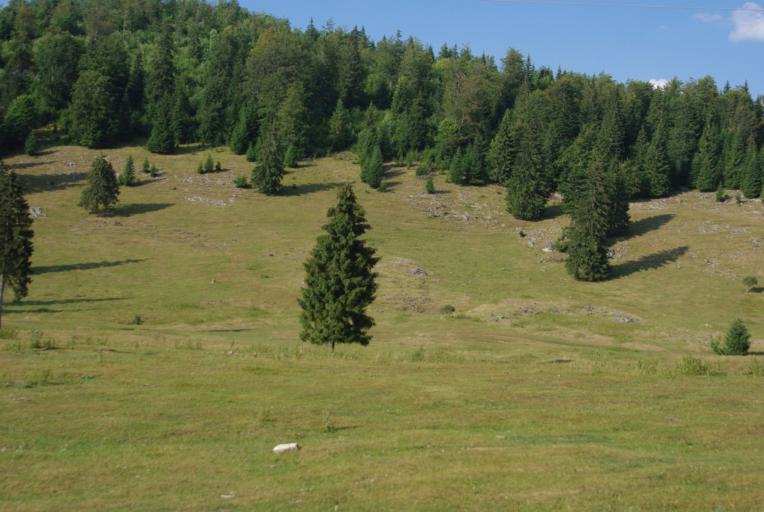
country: RO
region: Alba
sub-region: Comuna Arieseni
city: Arieseni
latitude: 46.5875
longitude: 22.6911
